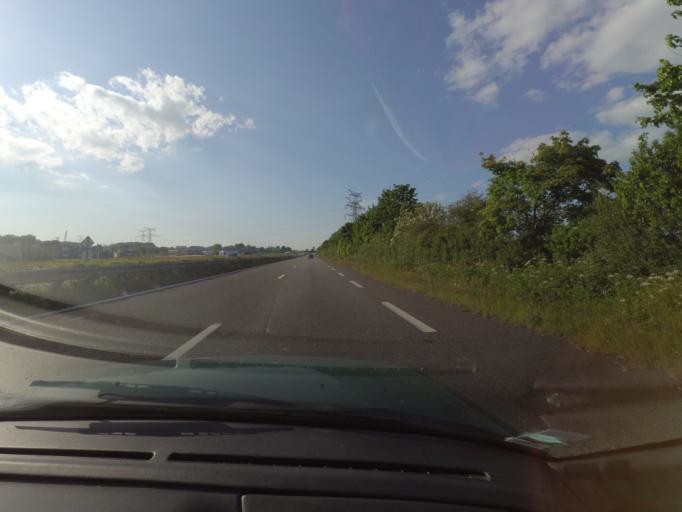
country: FR
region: Pays de la Loire
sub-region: Departement de la Vendee
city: Belleville-sur-Vie
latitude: 46.7909
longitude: -1.4249
